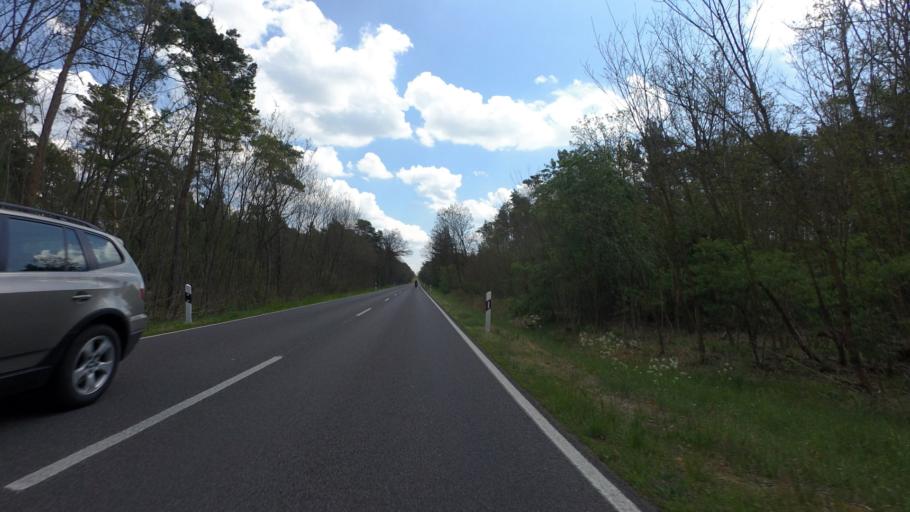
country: DE
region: Brandenburg
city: Neu Zauche
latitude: 51.9451
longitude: 14.0144
